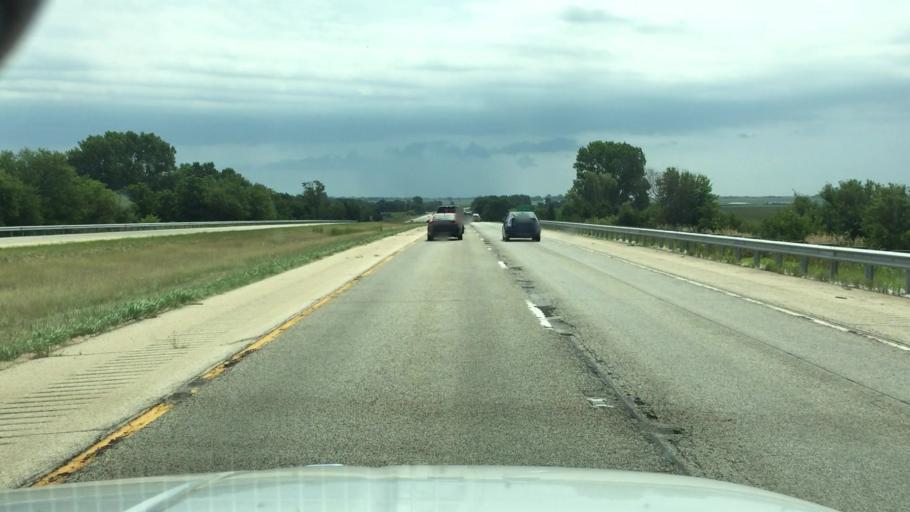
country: US
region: Illinois
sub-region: Peoria County
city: Elmwood
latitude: 40.8338
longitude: -89.8869
